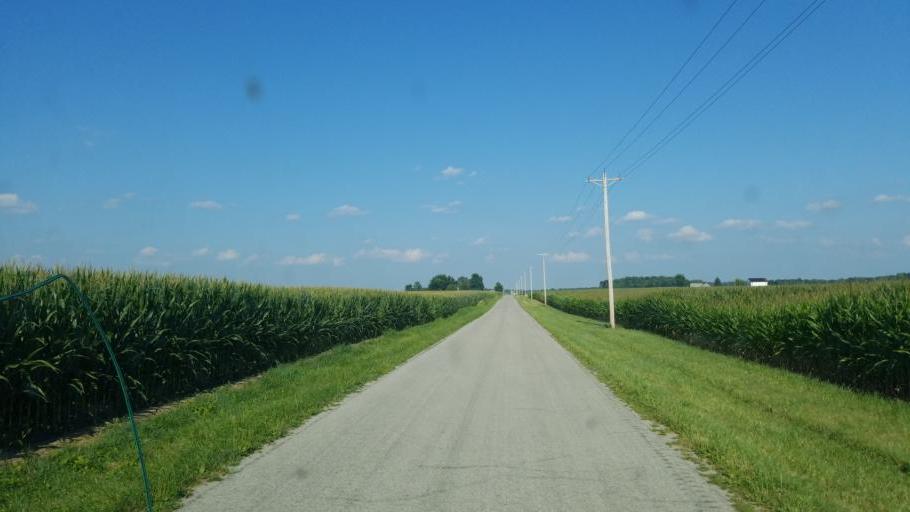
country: US
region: Ohio
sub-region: Wyandot County
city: Upper Sandusky
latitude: 40.7893
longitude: -83.1580
